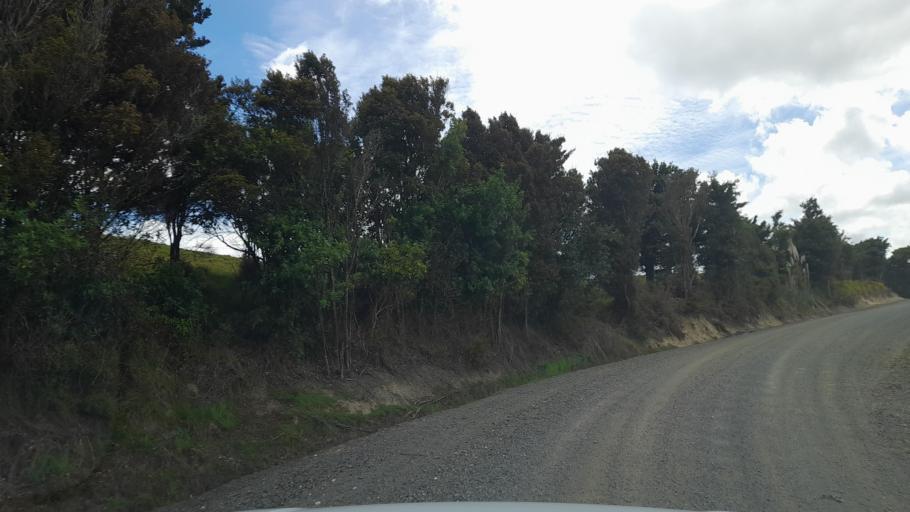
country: NZ
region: Auckland
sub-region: Auckland
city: Wellsford
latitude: -36.2026
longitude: 174.3365
